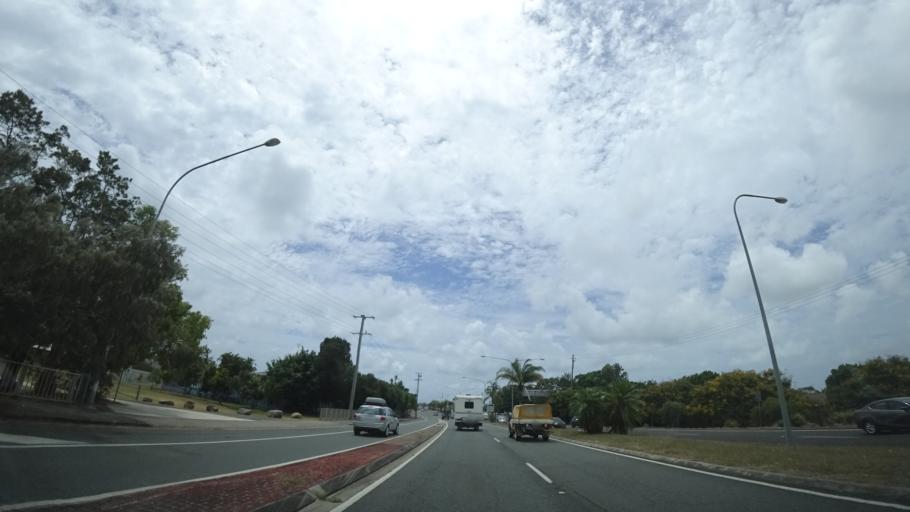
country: AU
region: Queensland
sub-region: Sunshine Coast
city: Mooloolaba
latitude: -26.6983
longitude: 153.1178
